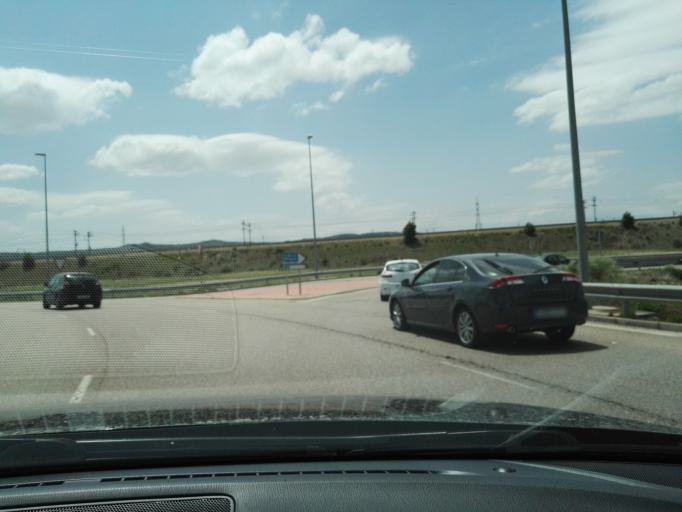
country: ES
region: Aragon
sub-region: Provincia de Zaragoza
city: Montecanal
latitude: 41.6281
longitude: -0.9903
